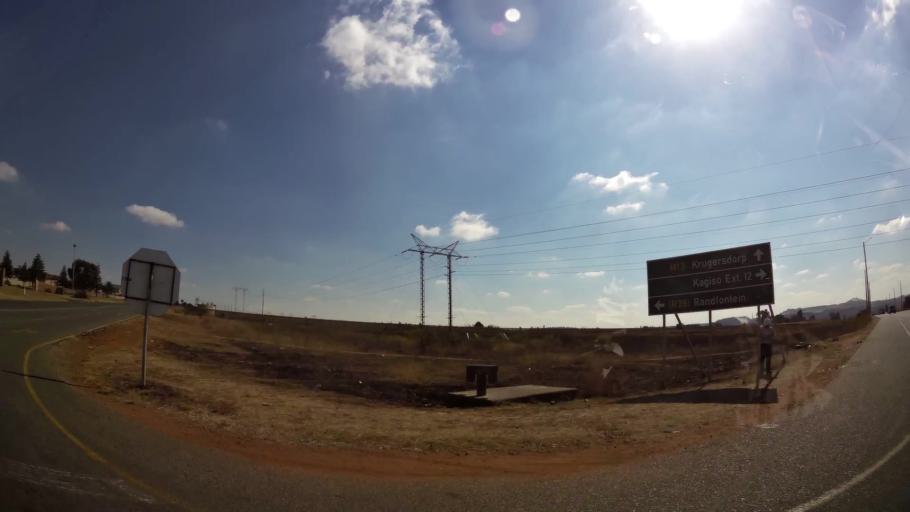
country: ZA
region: Gauteng
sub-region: West Rand District Municipality
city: Randfontein
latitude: -26.1635
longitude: 27.7614
